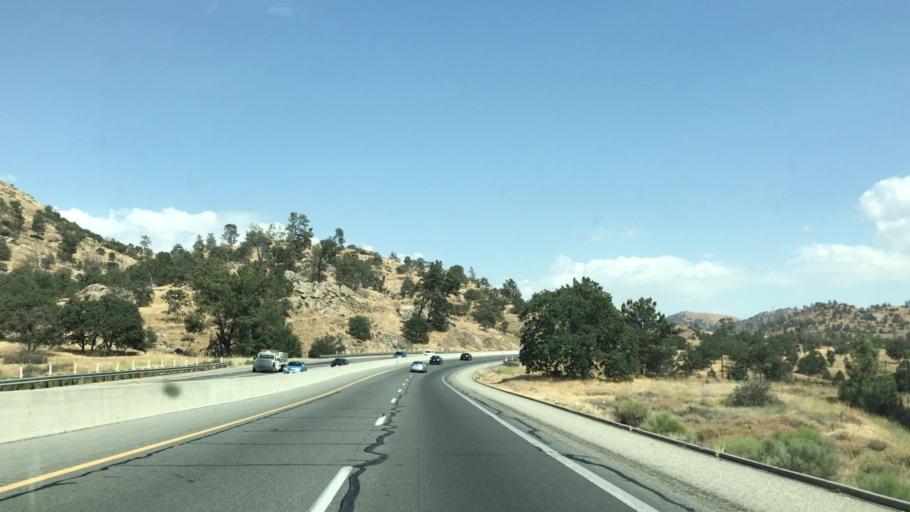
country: US
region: California
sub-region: Kern County
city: Golden Hills
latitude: 35.2083
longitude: -118.5372
